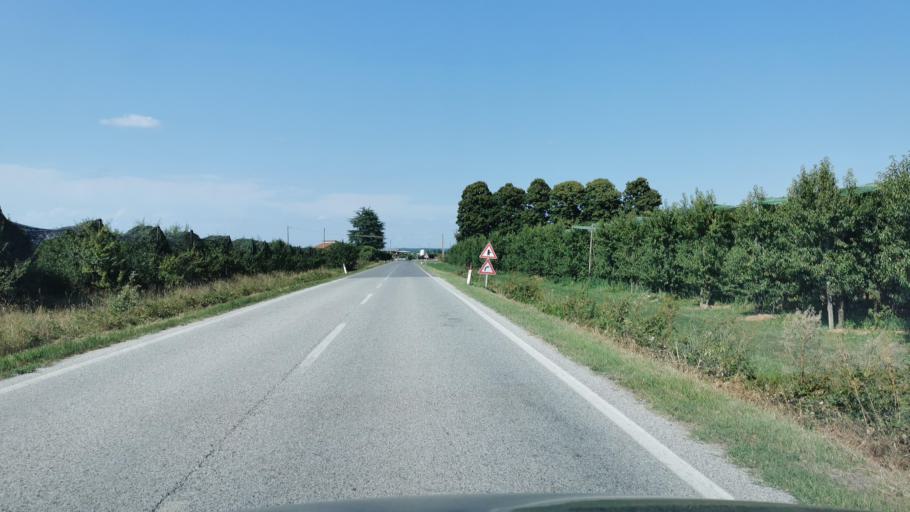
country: IT
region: Piedmont
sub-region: Provincia di Cuneo
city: Revello
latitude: 44.6676
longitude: 7.3975
